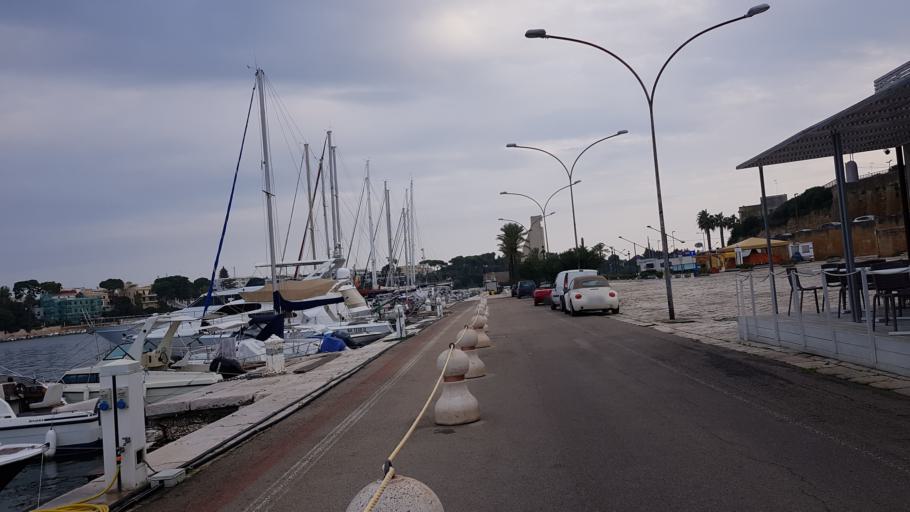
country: IT
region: Apulia
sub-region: Provincia di Brindisi
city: Brindisi
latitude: 40.6412
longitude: 17.9421
